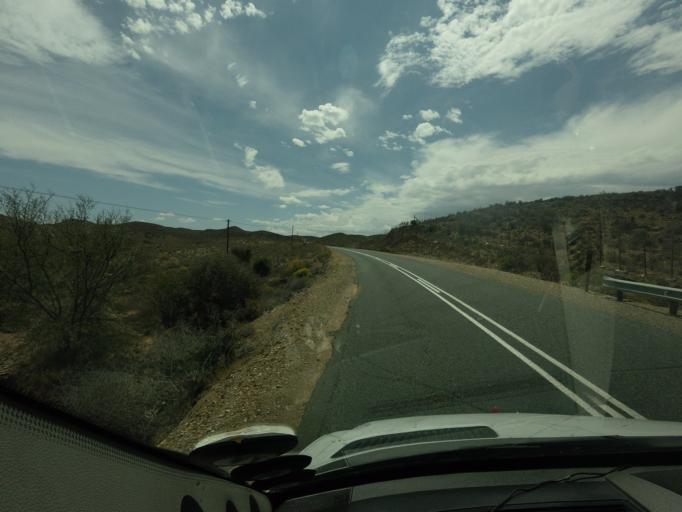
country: ZA
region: Western Cape
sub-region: Eden District Municipality
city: Ladismith
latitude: -33.7091
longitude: 20.9708
